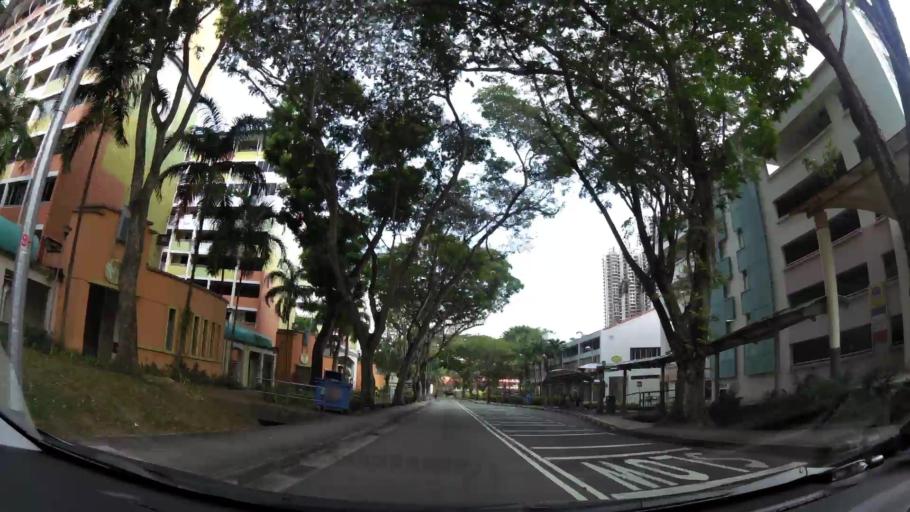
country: SG
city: Singapore
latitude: 1.2981
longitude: 103.7976
